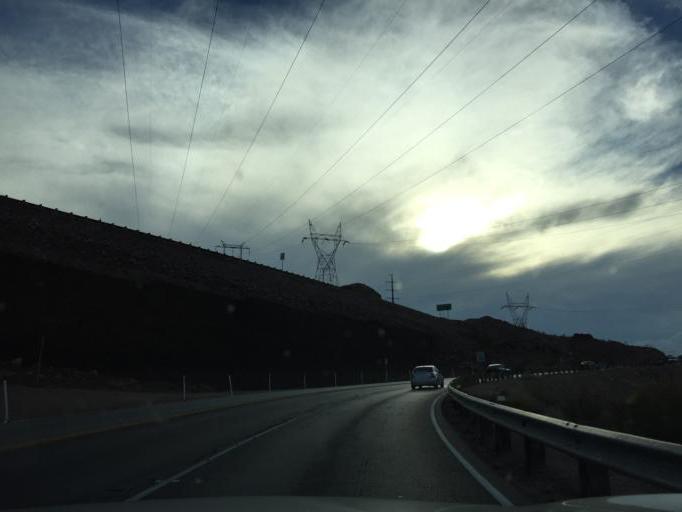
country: US
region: Nevada
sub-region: Clark County
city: Boulder City
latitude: 36.0156
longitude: -114.7471
